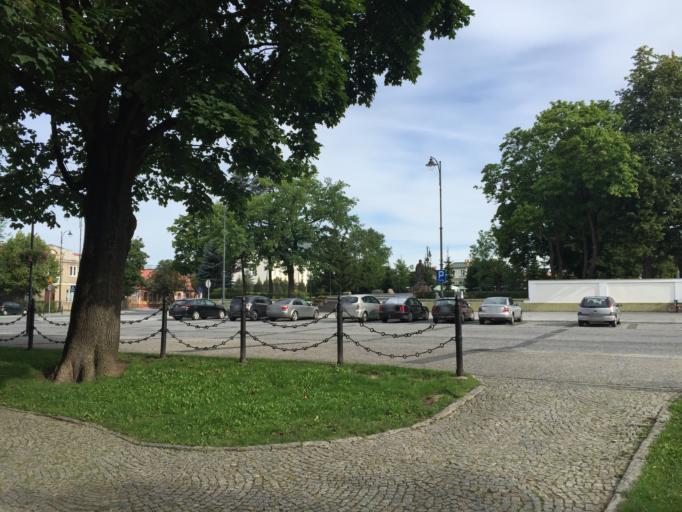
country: PL
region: Podlasie
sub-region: Suwalki
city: Suwalki
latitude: 54.1011
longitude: 22.9266
